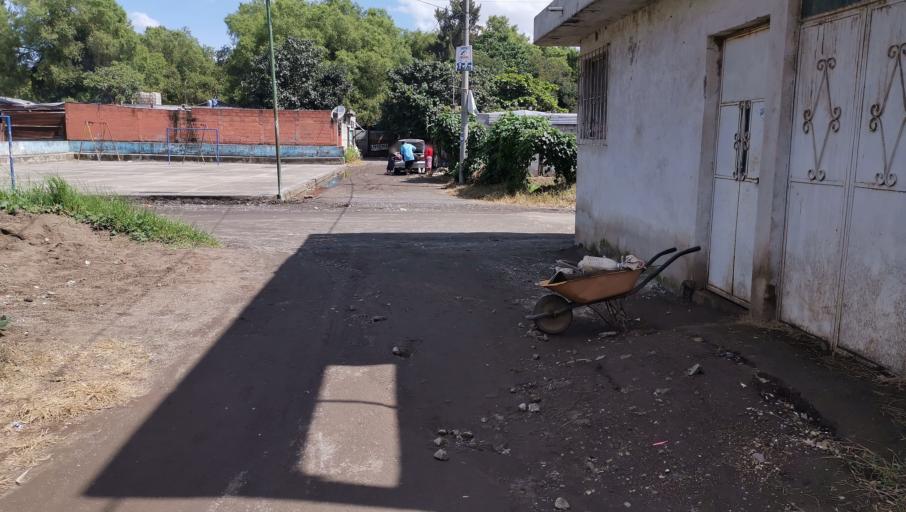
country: GT
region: Escuintla
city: San Vicente Pacaya
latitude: 14.4445
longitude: -90.6328
